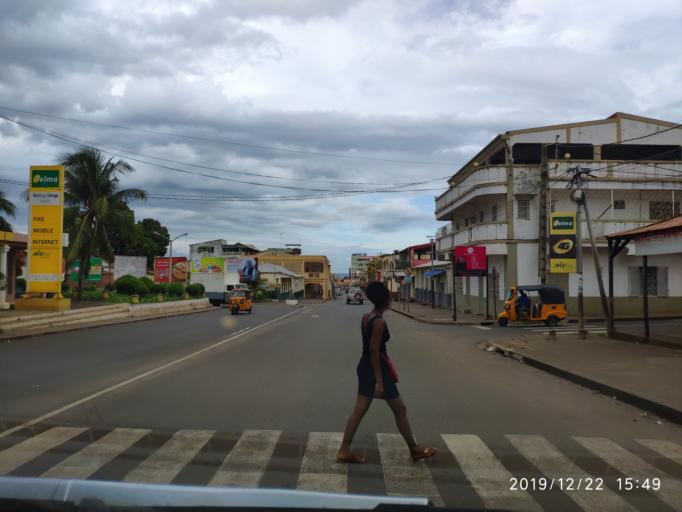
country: MG
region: Diana
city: Antsiranana
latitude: -12.2781
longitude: 49.2916
